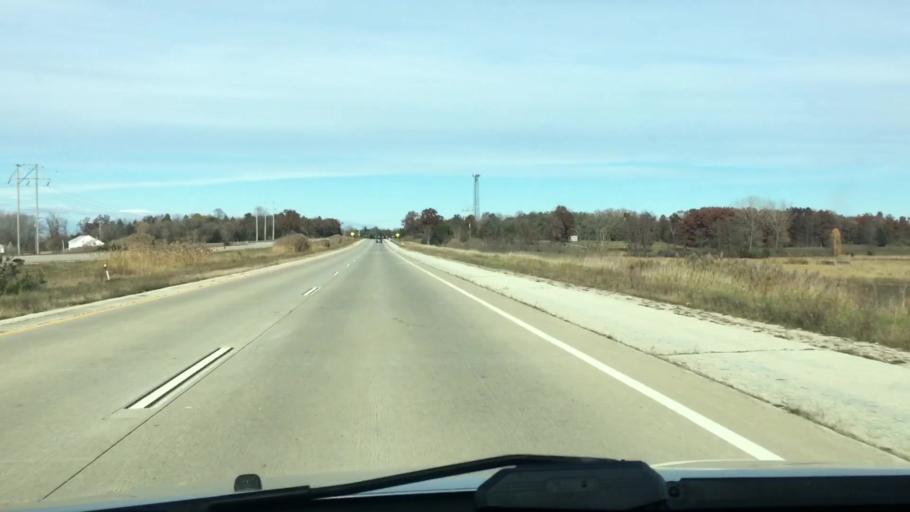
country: US
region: Wisconsin
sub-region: Brown County
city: Bellevue
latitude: 44.5901
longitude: -87.8651
